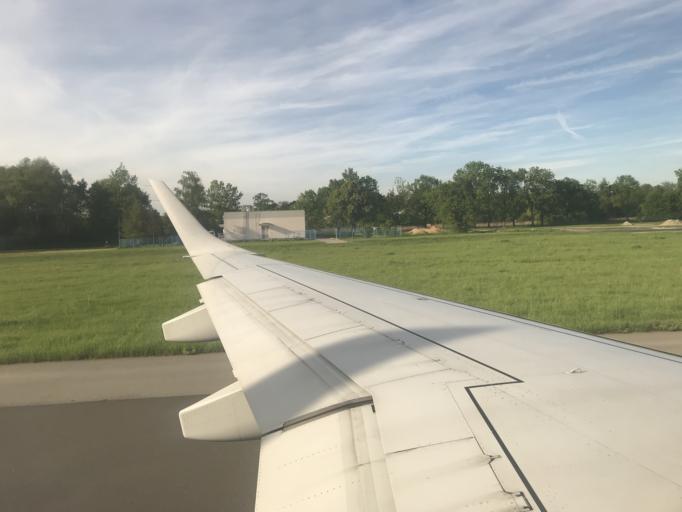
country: PL
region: Lower Silesian Voivodeship
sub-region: Powiat wroclawski
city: Smolec
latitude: 51.1043
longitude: 16.8920
